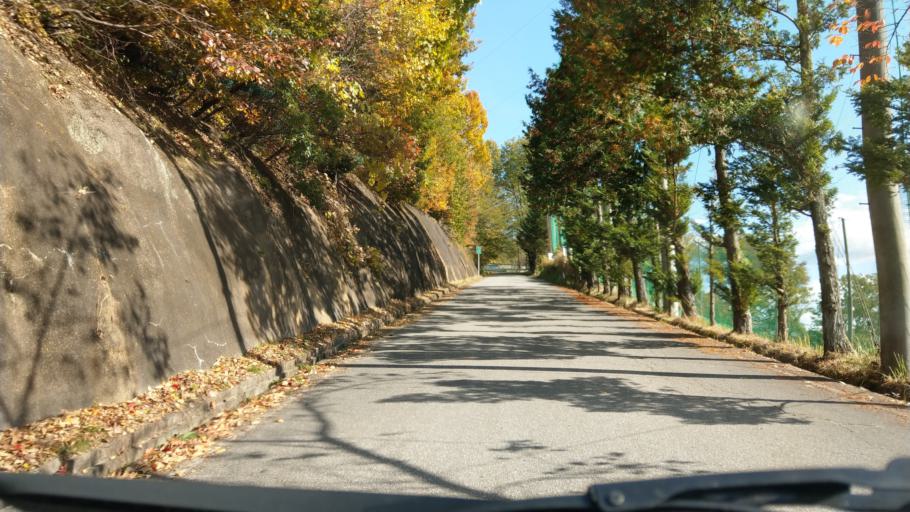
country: JP
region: Nagano
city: Komoro
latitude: 36.3074
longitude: 138.4311
